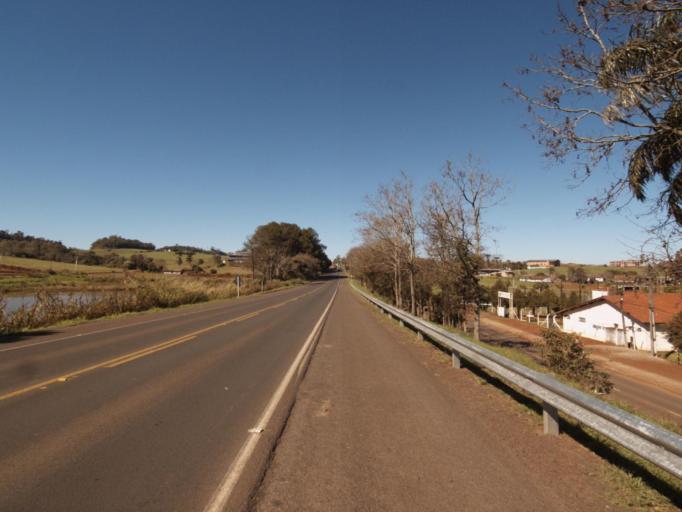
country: BR
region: Santa Catarina
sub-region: Chapeco
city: Chapeco
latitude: -26.8298
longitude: -52.9967
